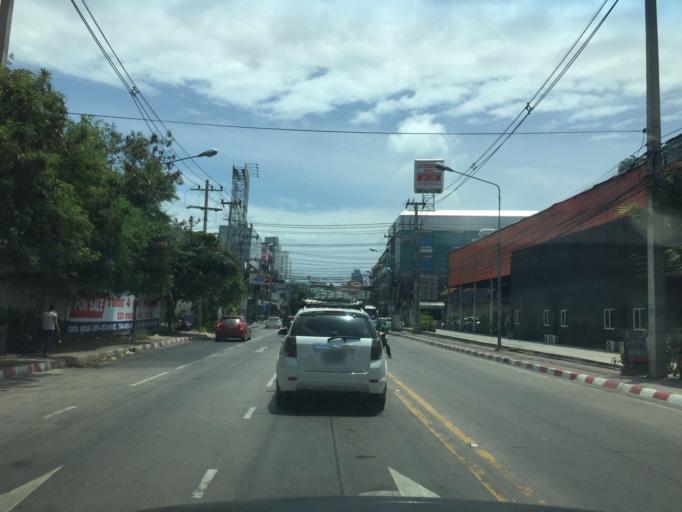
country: TH
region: Chon Buri
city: Phatthaya
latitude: 12.9228
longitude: 100.8822
